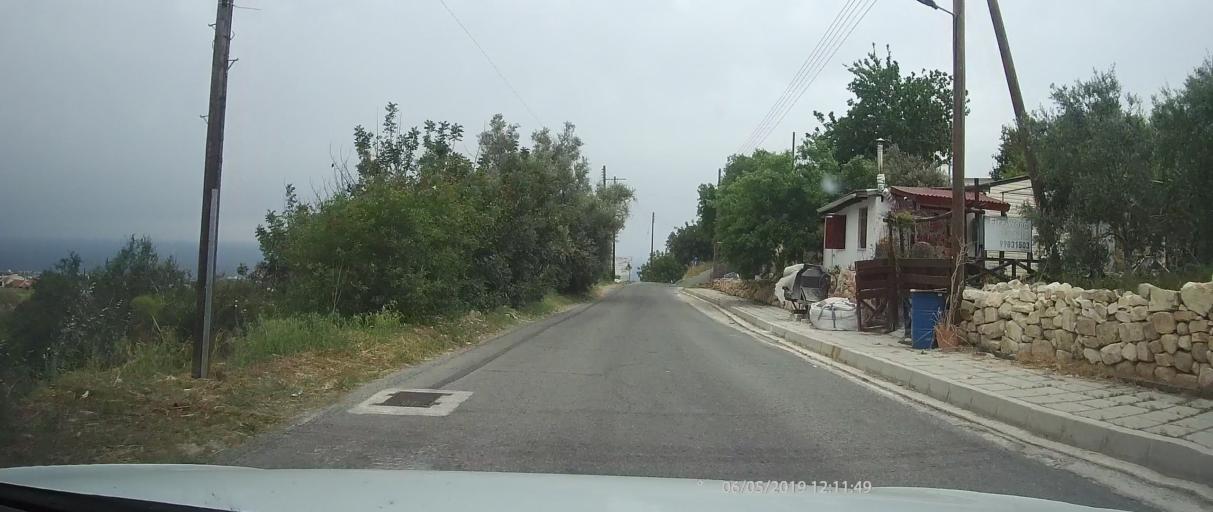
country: CY
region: Pafos
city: Tala
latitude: 34.8390
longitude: 32.4298
